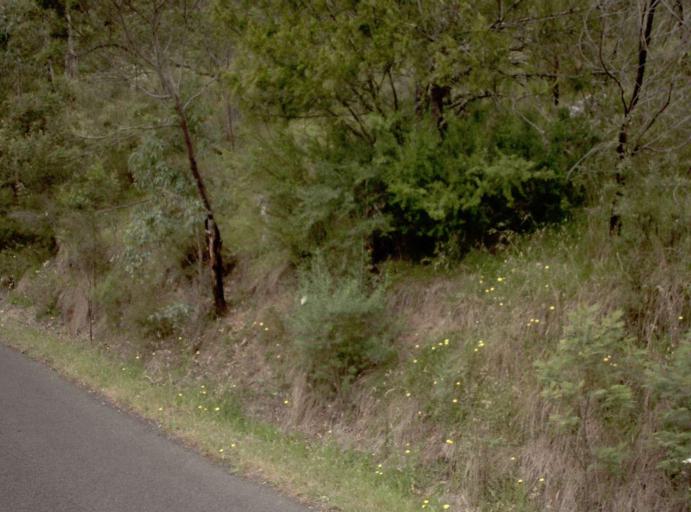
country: AU
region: Victoria
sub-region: East Gippsland
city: Bairnsdale
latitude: -37.4768
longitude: 147.2130
